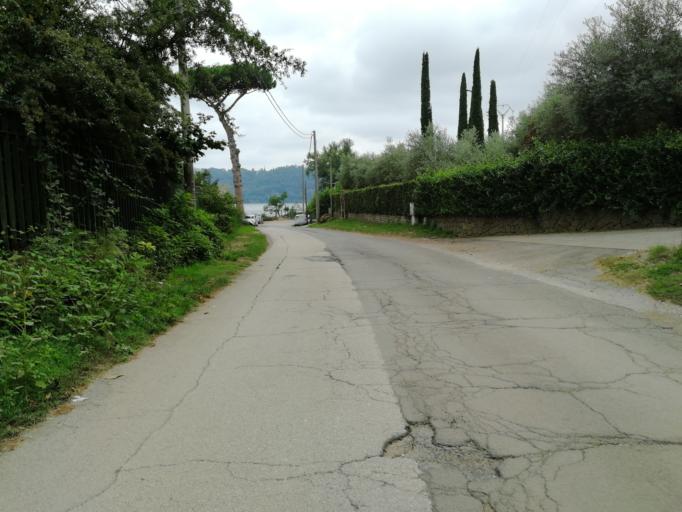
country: IT
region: Latium
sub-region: Citta metropolitana di Roma Capitale
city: Nemi
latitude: 41.7224
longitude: 12.7012
